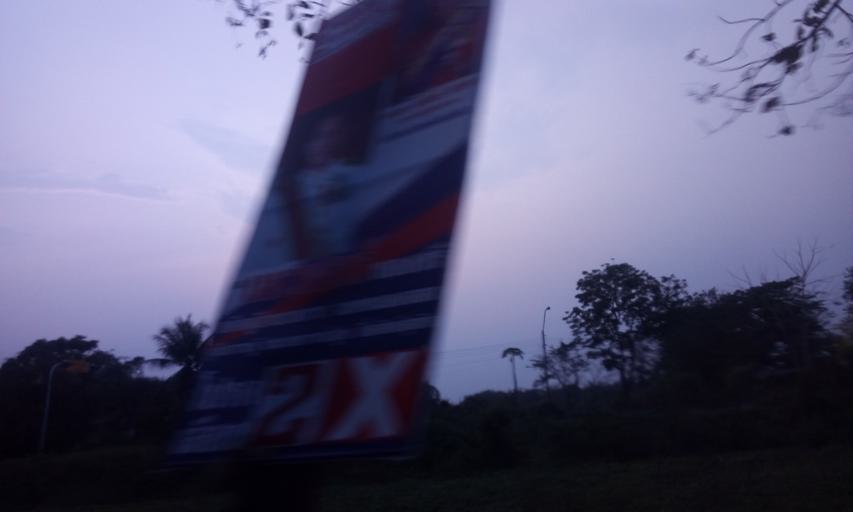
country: TH
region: Bangkok
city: Nong Chok
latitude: 13.9054
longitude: 100.8892
